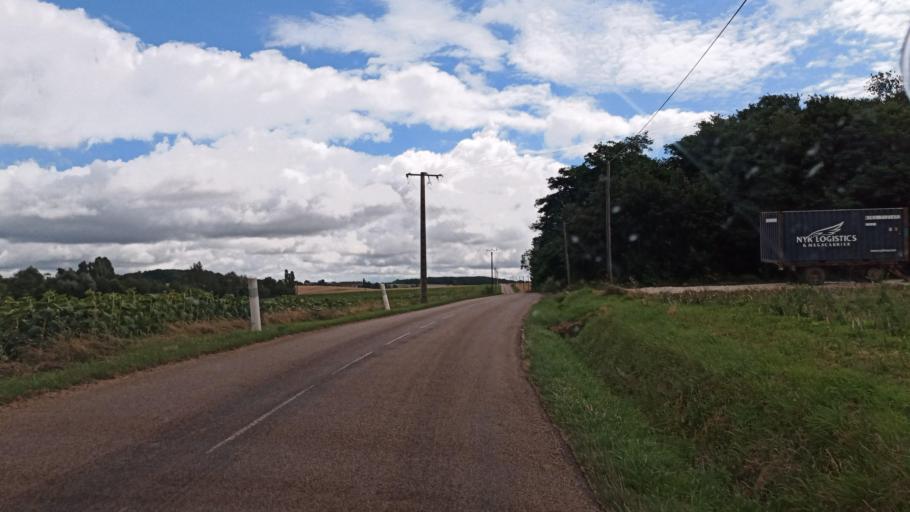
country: FR
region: Bourgogne
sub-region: Departement de l'Yonne
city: Cheroy
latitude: 48.2365
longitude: 3.0539
